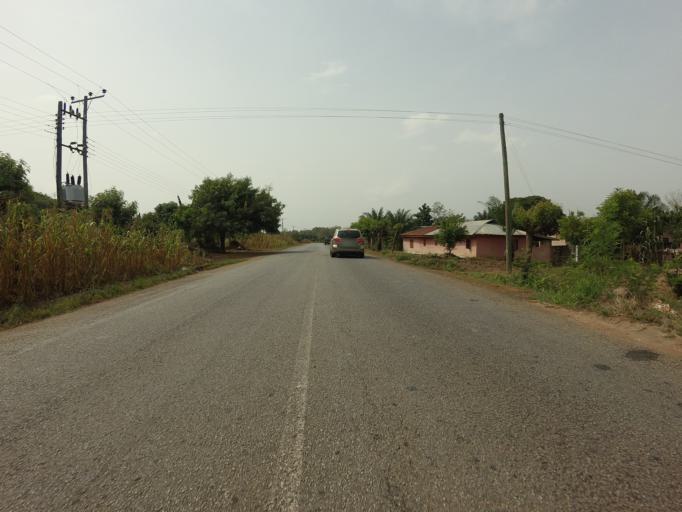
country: GH
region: Volta
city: Ho
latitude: 6.3429
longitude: 0.1736
